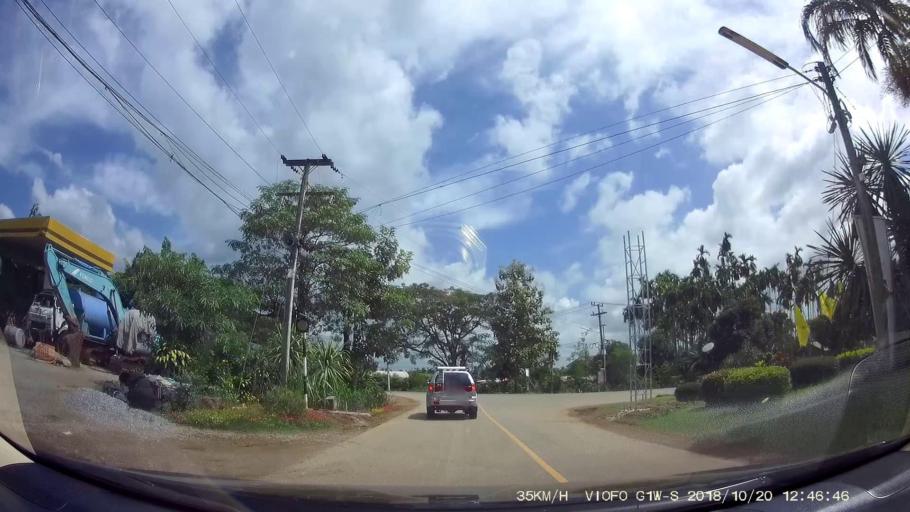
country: TH
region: Chaiyaphum
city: Khon San
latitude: 16.5328
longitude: 101.8822
